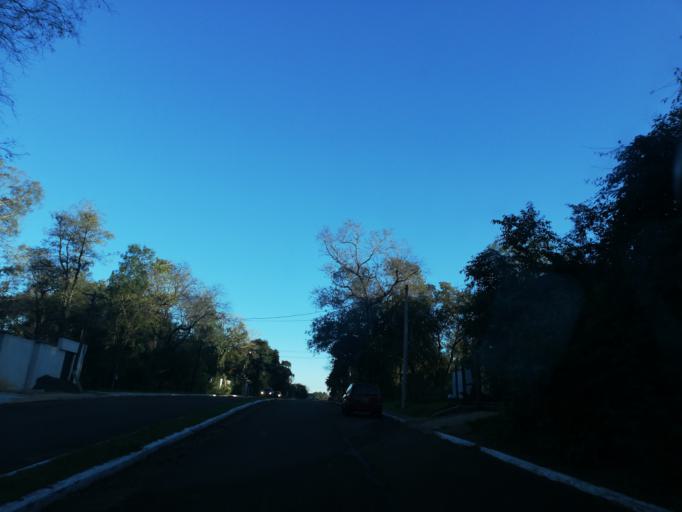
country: AR
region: Misiones
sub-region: Departamento de Candelaria
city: Candelaria
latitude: -27.4495
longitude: -55.7471
